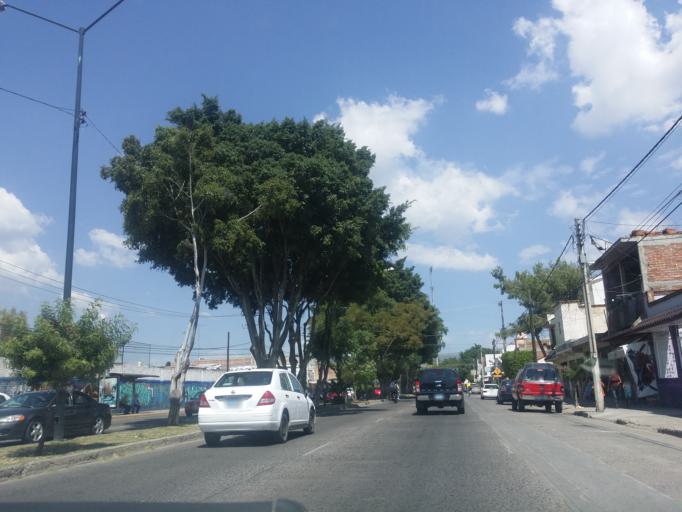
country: MX
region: Guanajuato
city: Leon
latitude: 21.1446
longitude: -101.6525
